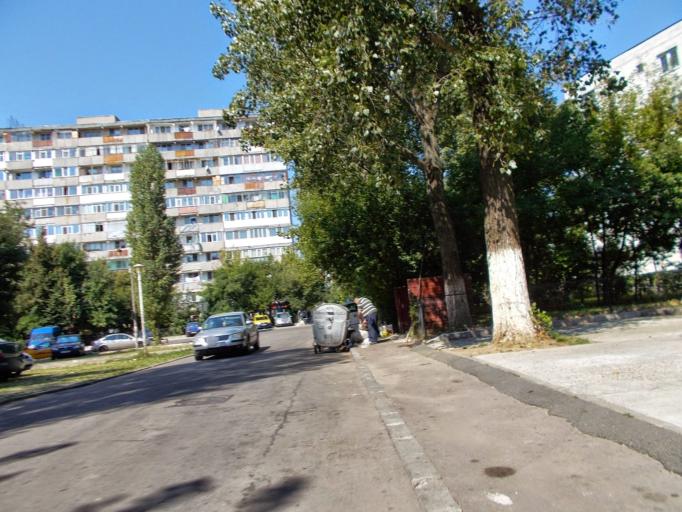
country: RO
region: Bucuresti
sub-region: Municipiul Bucuresti
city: Bucuresti
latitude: 44.3799
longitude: 26.1043
